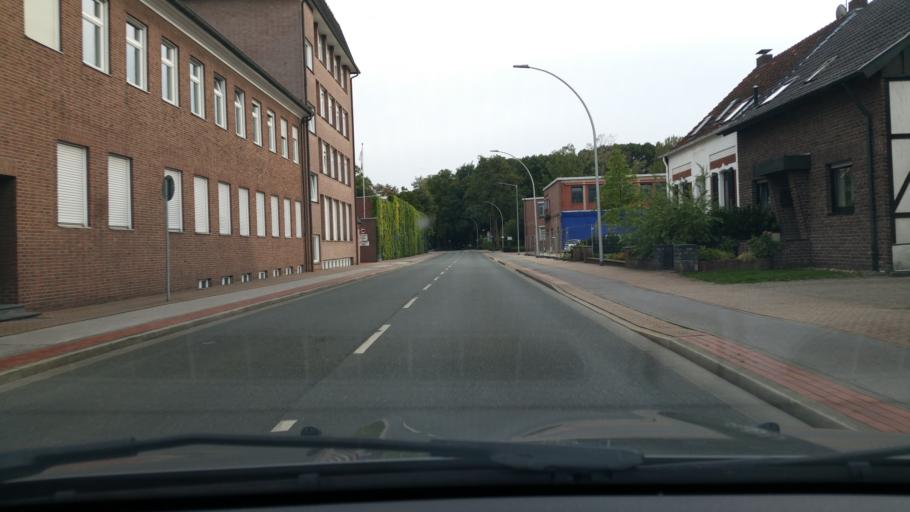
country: DE
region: North Rhine-Westphalia
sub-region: Regierungsbezirk Dusseldorf
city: Bocholt
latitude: 51.8464
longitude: 6.6196
